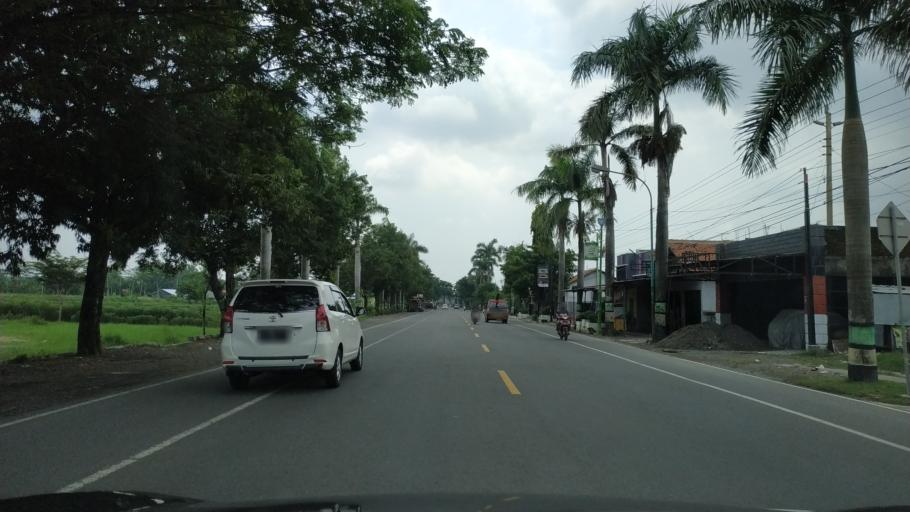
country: ID
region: Central Java
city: Slawi
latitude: -7.0045
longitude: 109.1406
